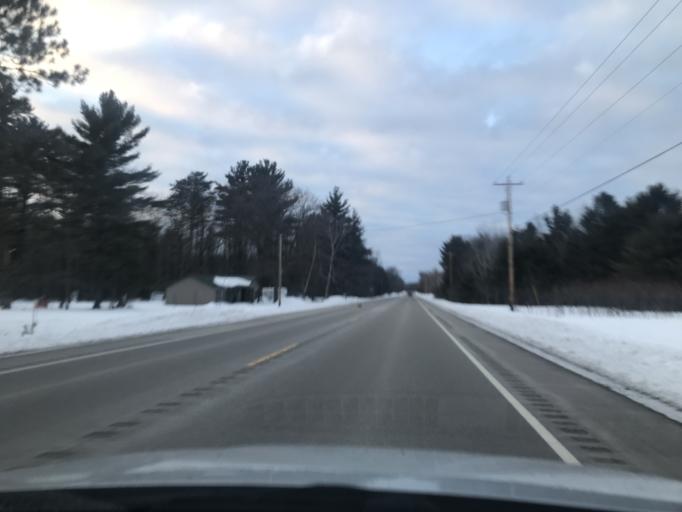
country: US
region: Wisconsin
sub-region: Marinette County
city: Marinette
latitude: 45.1464
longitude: -87.6991
